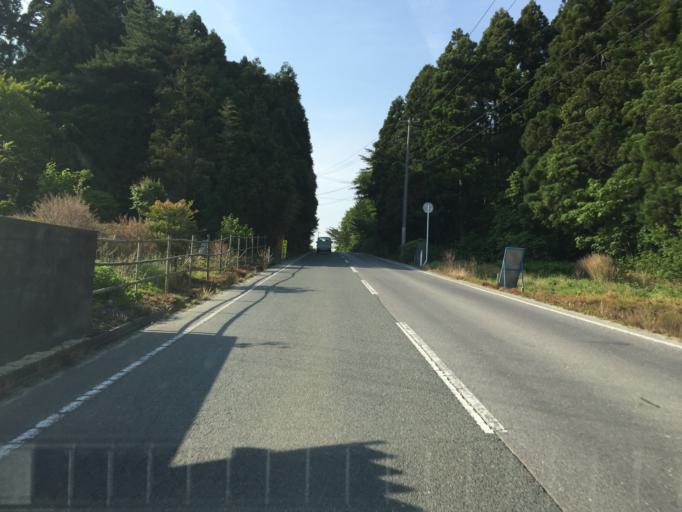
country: JP
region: Fukushima
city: Namie
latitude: 37.7414
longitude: 141.0052
